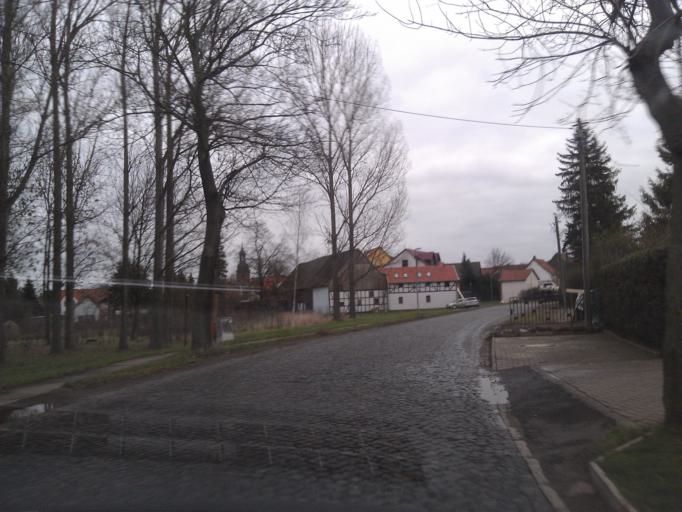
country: DE
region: Thuringia
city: Friemar
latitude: 50.9781
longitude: 10.7819
